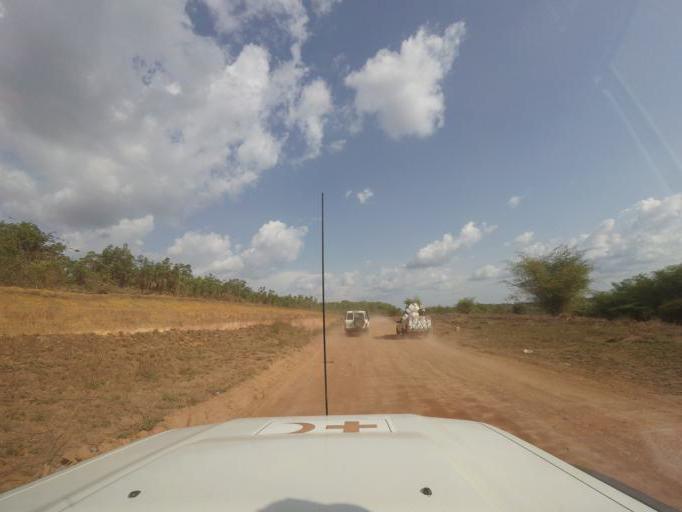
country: LR
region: Bong
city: Gbarnga
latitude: 7.0403
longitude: -9.5148
